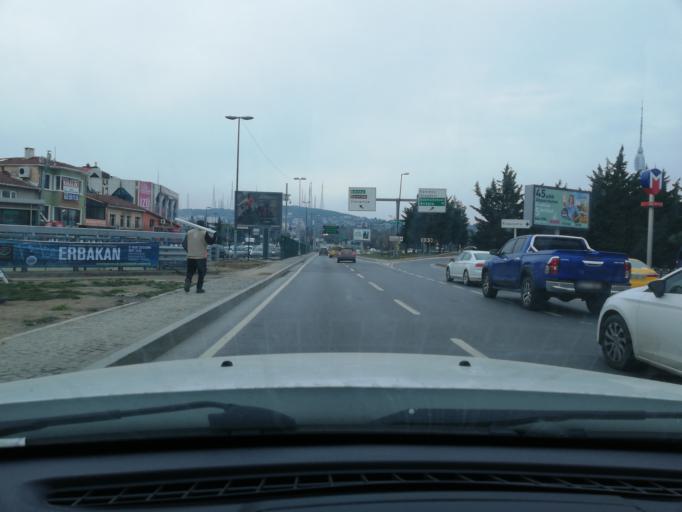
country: TR
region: Istanbul
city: UEskuedar
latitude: 41.0224
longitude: 29.0453
